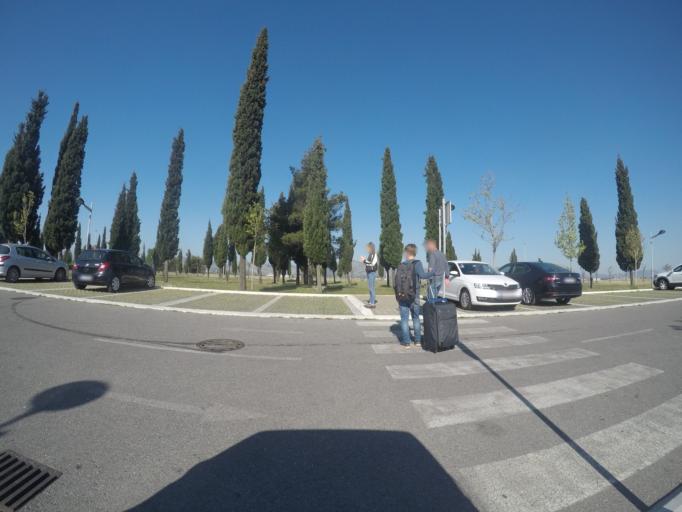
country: ME
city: Mojanovici
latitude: 42.3677
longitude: 19.2454
